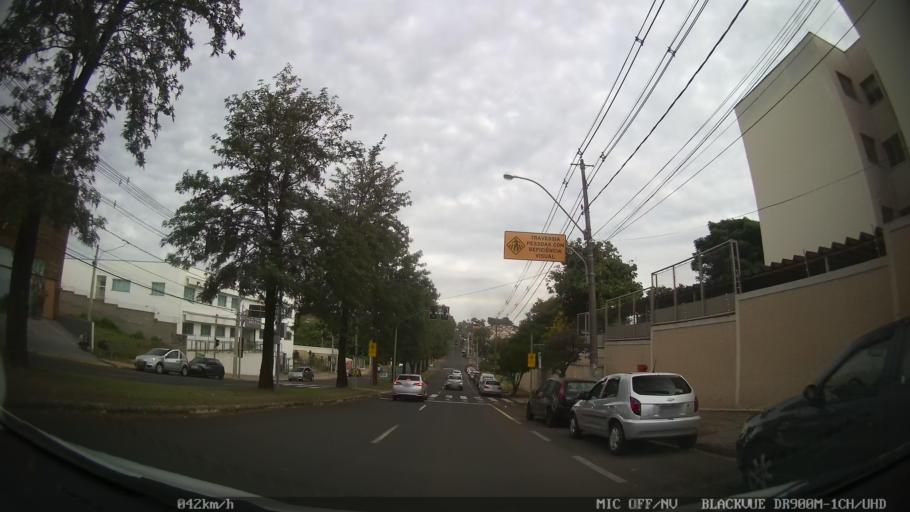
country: BR
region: Sao Paulo
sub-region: Piracicaba
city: Piracicaba
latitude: -22.7319
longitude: -47.6218
